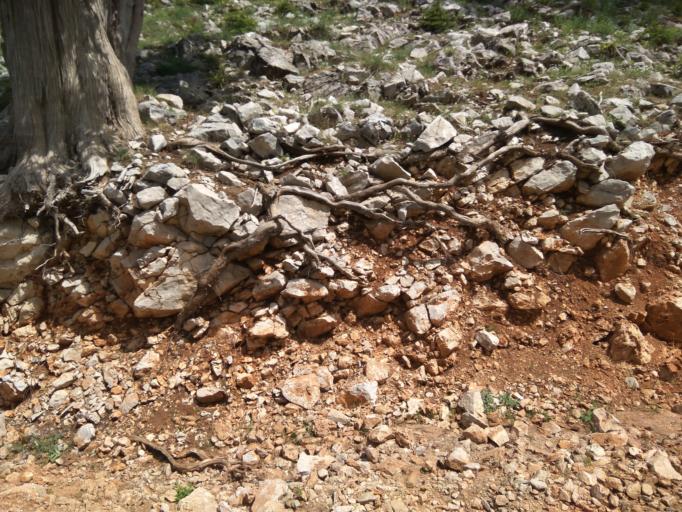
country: TR
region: Antalya
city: Altinyaka
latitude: 36.5473
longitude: 30.4144
